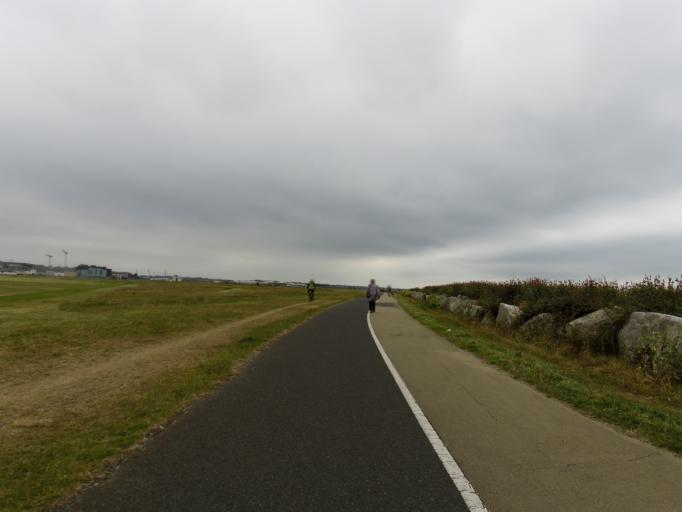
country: IE
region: Connaught
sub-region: County Galway
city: Gaillimh
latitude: 53.2633
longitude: -9.0559
